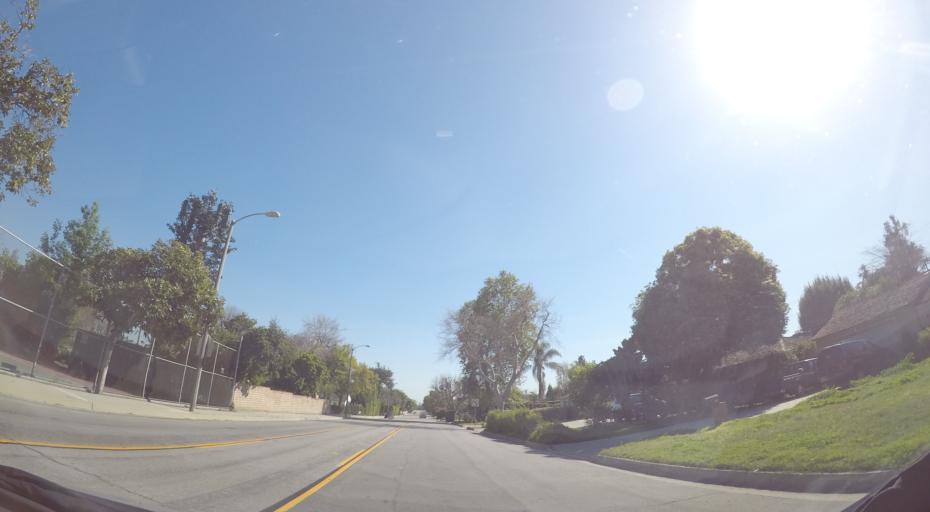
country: US
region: California
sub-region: Los Angeles County
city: Sierra Madre
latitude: 34.1383
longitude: -118.0676
